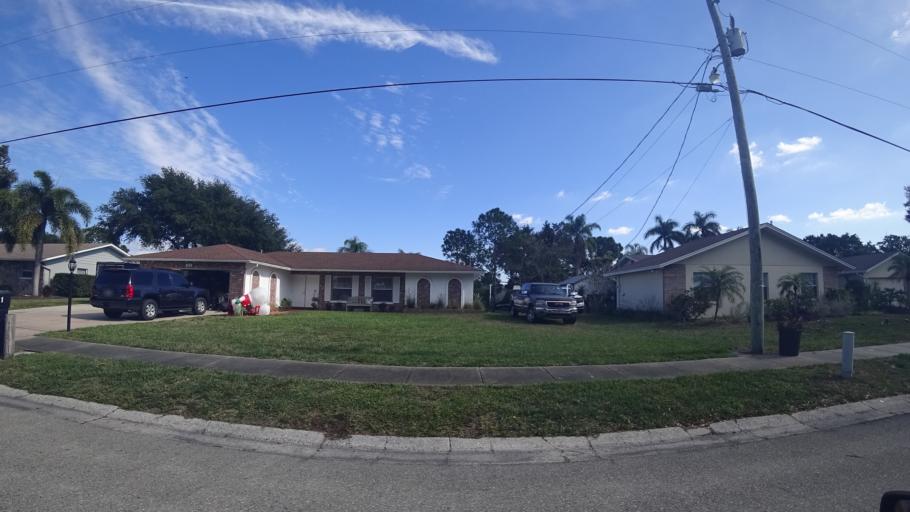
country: US
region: Florida
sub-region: Manatee County
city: West Bradenton
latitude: 27.5020
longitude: -82.6273
